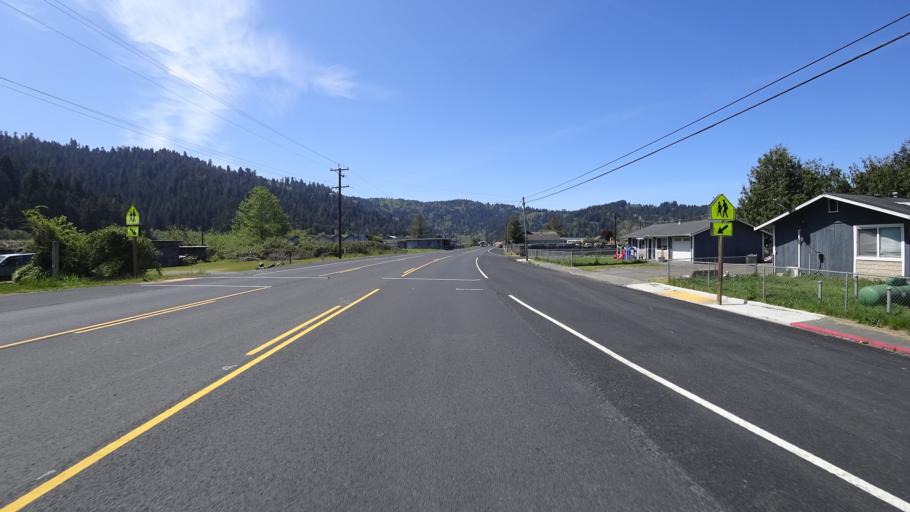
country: US
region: California
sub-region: Humboldt County
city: Westhaven-Moonstone
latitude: 41.2870
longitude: -124.0594
